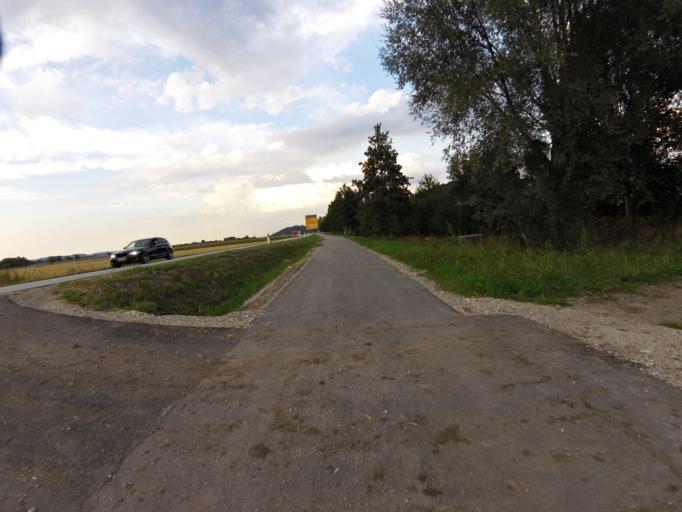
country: DE
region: Bavaria
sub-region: Upper Bavaria
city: Langenpreising
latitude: 48.4597
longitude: 12.0034
